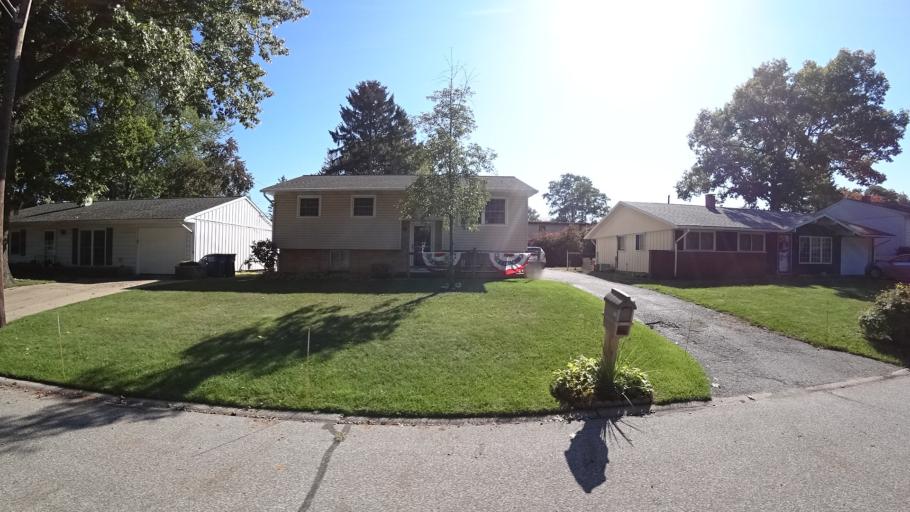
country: US
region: Indiana
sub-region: LaPorte County
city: Michigan City
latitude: 41.6898
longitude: -86.9023
